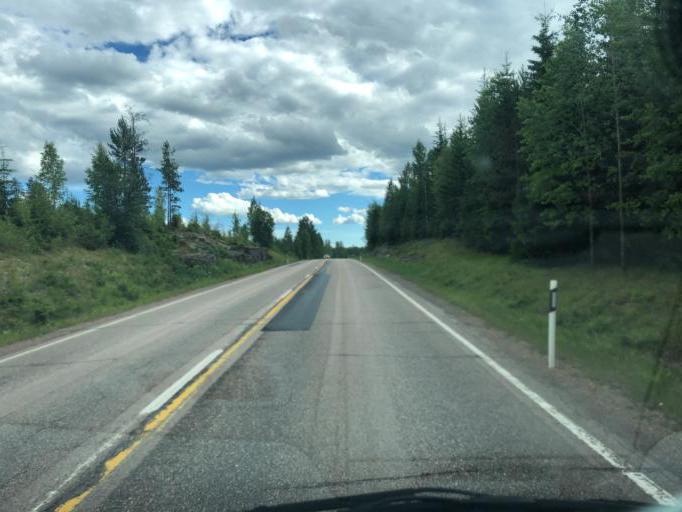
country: FI
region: Southern Savonia
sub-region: Mikkeli
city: Maentyharju
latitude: 61.1318
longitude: 27.1029
